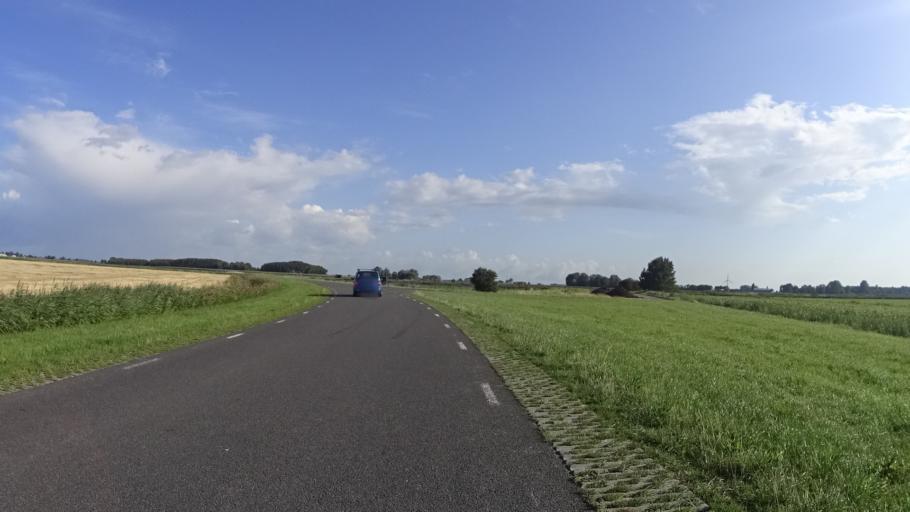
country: NL
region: Friesland
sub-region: Gemeente Harlingen
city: Harlingen
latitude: 53.1271
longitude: 5.4578
